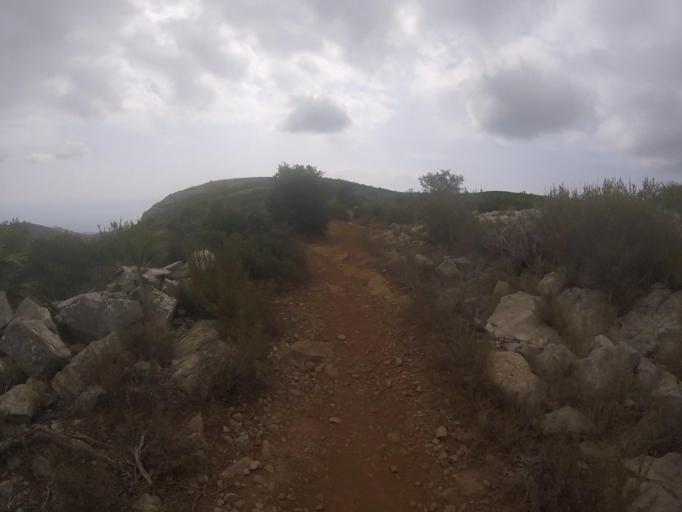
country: ES
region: Valencia
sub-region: Provincia de Castello
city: Santa Magdalena de Pulpis
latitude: 40.3478
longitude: 0.3459
